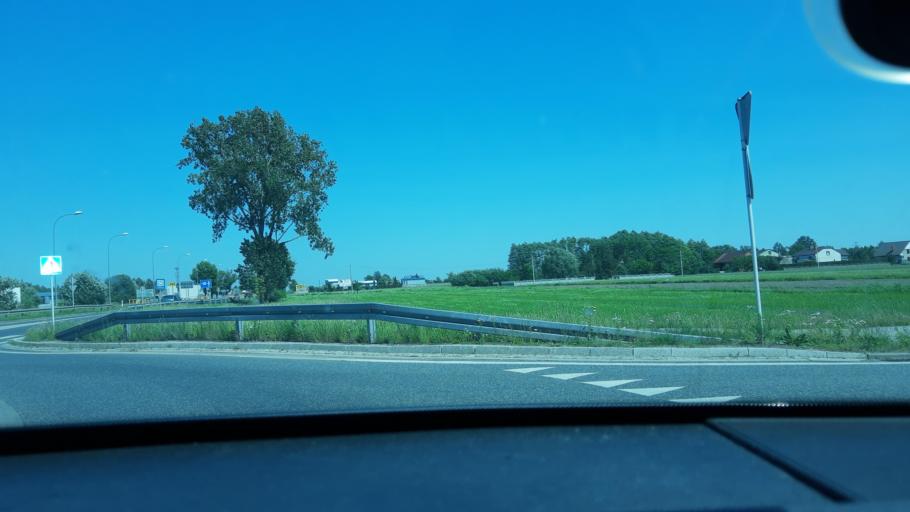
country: PL
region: Lodz Voivodeship
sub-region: Powiat zdunskowolski
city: Zapolice
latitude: 51.6067
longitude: 18.8760
